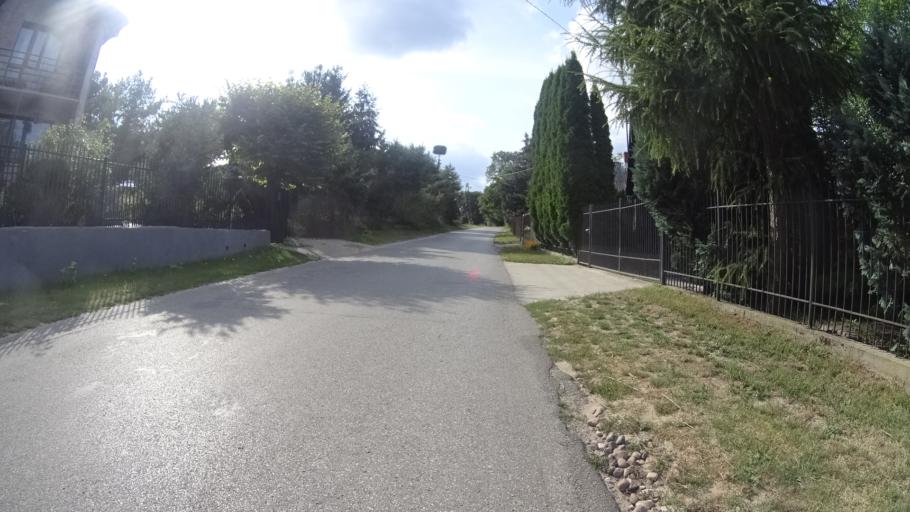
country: PL
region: Masovian Voivodeship
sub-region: Powiat grojecki
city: Mogielnica
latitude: 51.6547
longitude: 20.7638
